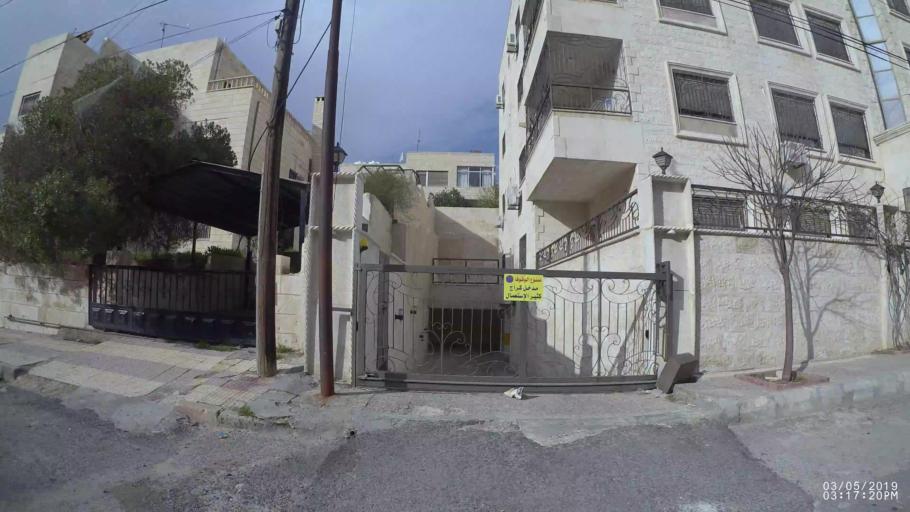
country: JO
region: Amman
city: Amman
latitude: 32.0035
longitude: 35.9462
